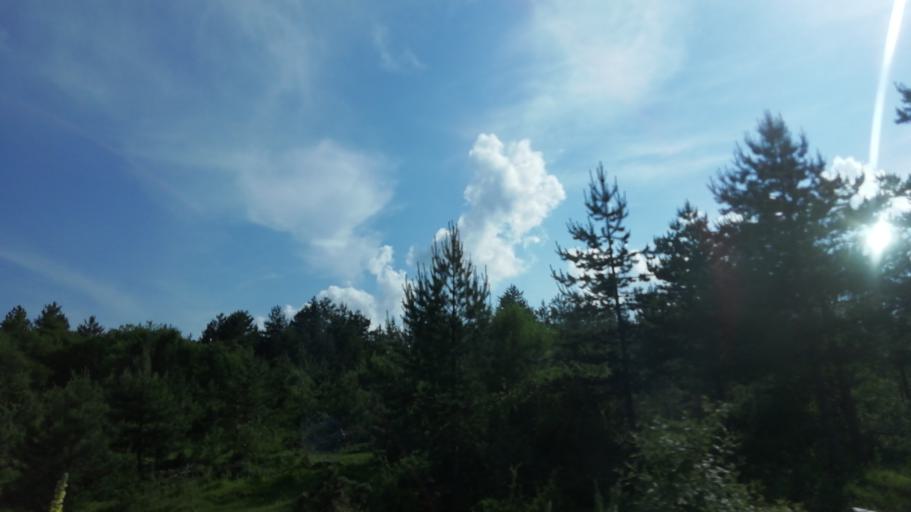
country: TR
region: Karabuk
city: Karabuk
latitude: 41.0859
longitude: 32.5775
